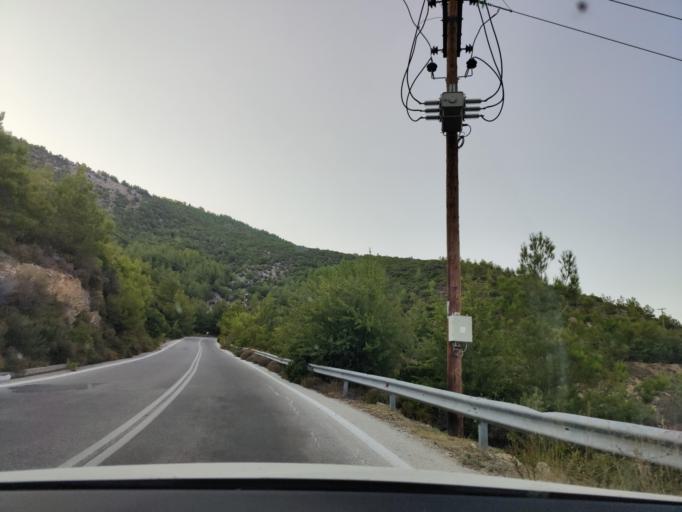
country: GR
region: East Macedonia and Thrace
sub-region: Nomos Kavalas
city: Potamia
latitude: 40.6201
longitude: 24.7596
